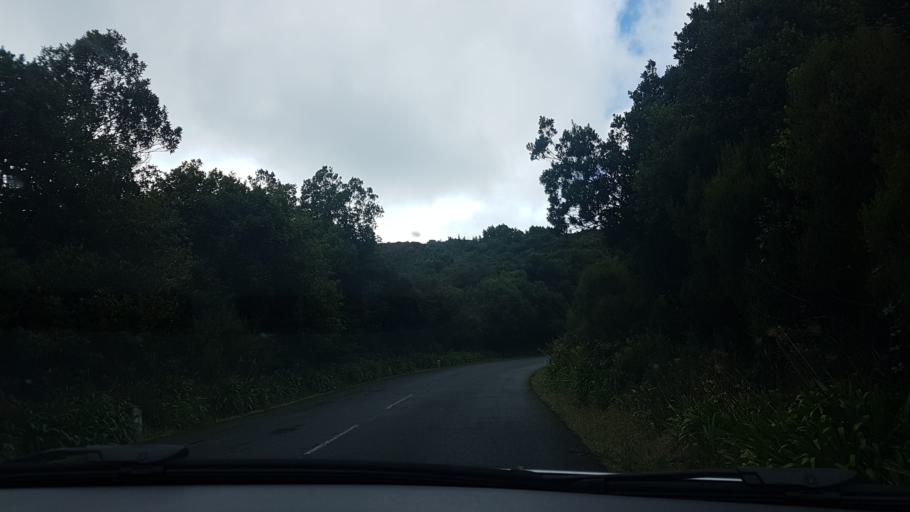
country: PT
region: Madeira
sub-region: Sao Vicente
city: Sao Vicente
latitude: 32.7584
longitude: -17.0164
